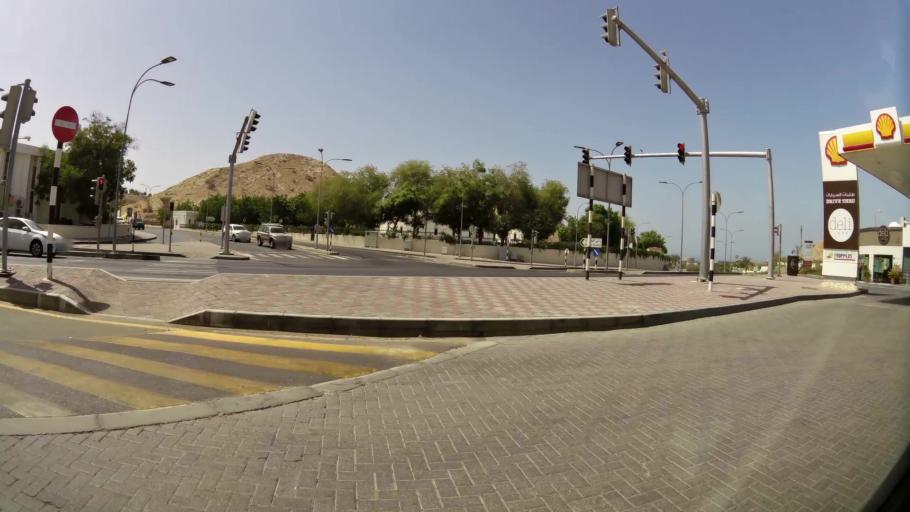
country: OM
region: Muhafazat Masqat
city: Muscat
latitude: 23.6227
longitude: 58.5068
